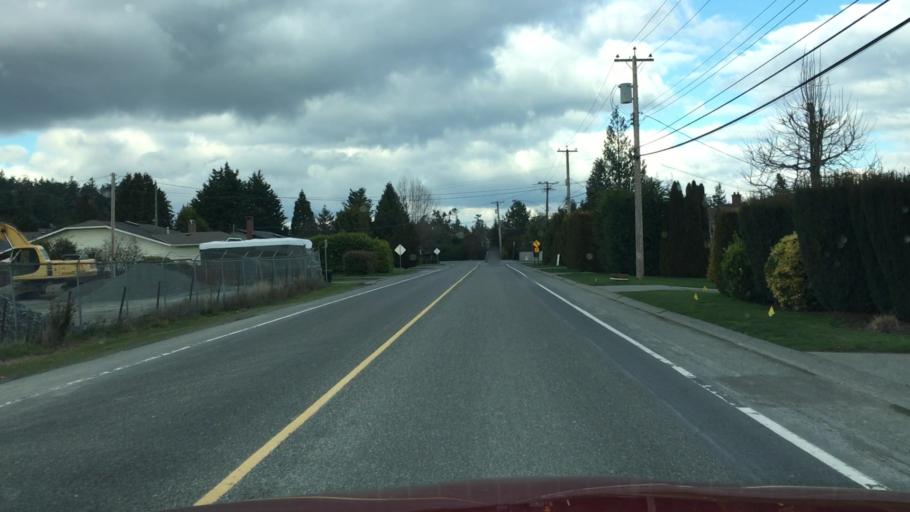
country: CA
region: British Columbia
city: North Saanich
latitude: 48.5978
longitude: -123.3946
